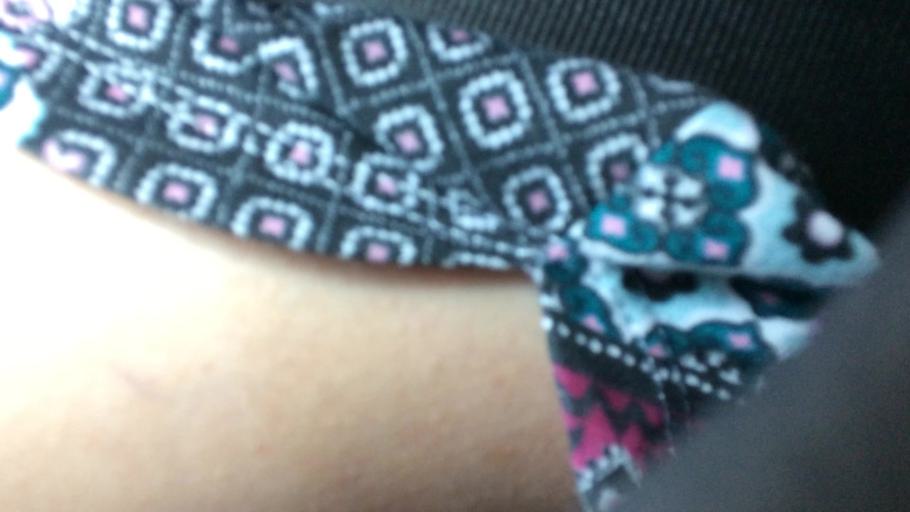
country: US
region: New Mexico
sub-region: Colfax County
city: Springer
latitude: 36.2056
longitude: -104.6631
